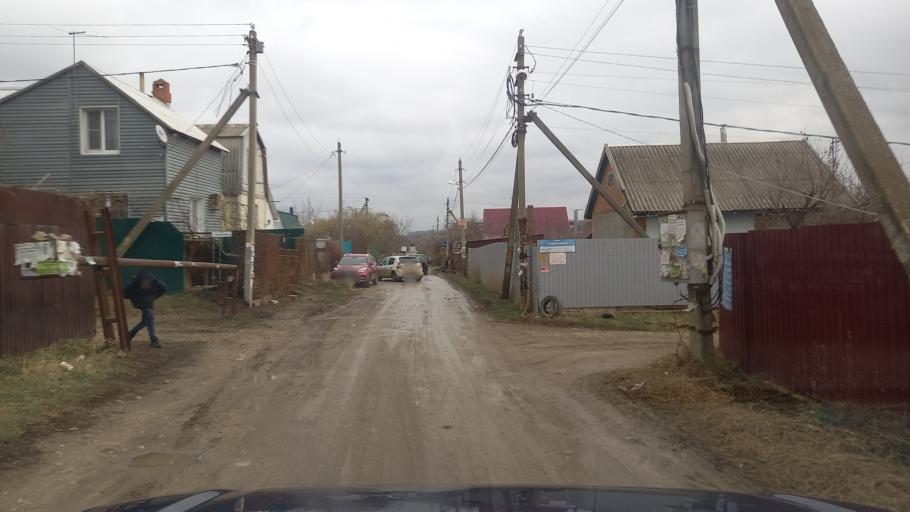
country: RU
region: Krasnodarskiy
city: Pashkovskiy
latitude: 45.0551
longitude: 39.1741
